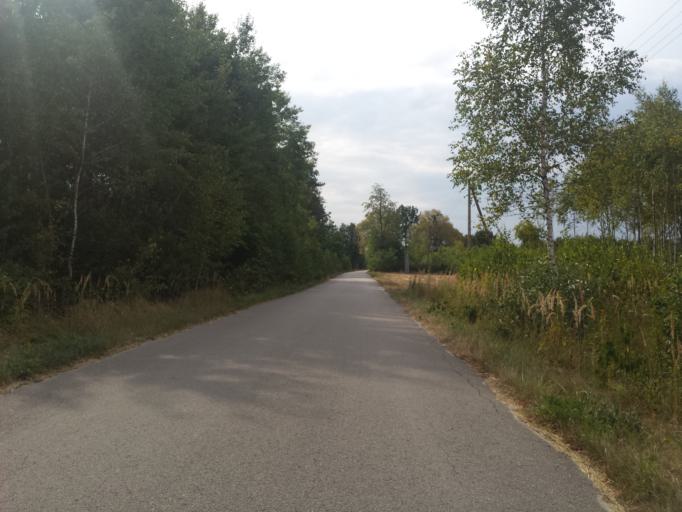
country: PL
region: Swietokrzyskie
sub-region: Powiat kielecki
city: Rakow
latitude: 50.6676
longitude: 21.1329
